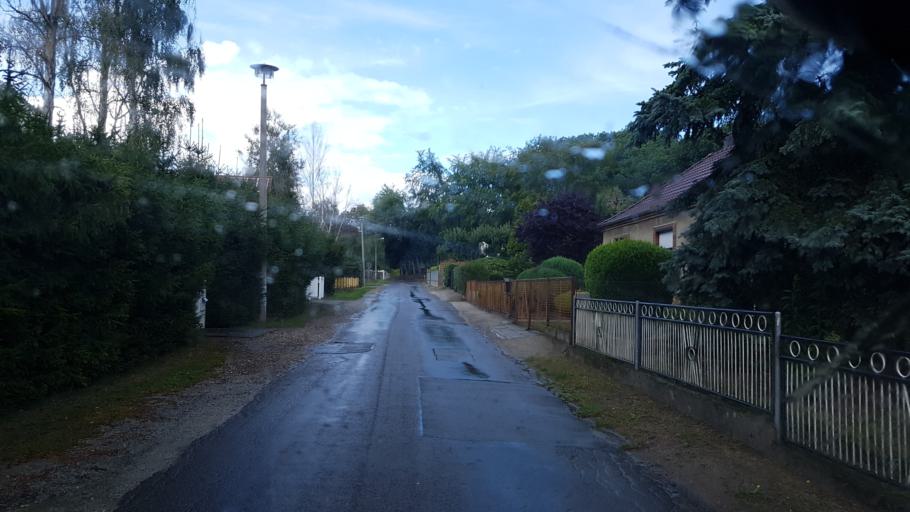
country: DE
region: Brandenburg
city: Tschernitz
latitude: 51.6094
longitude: 14.5932
